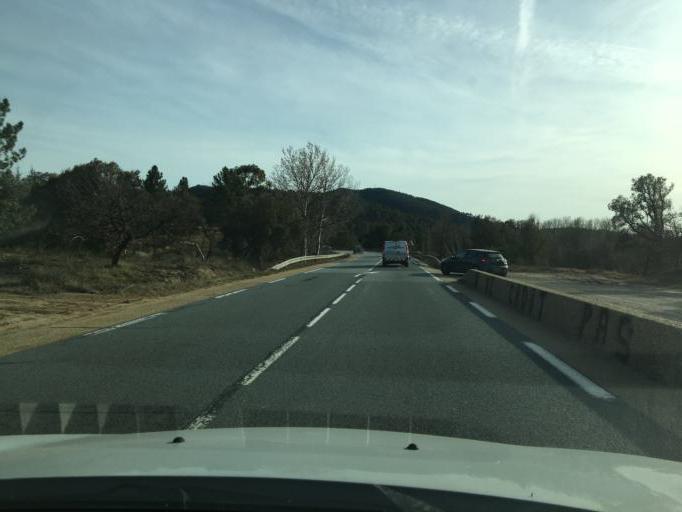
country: FR
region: Provence-Alpes-Cote d'Azur
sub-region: Departement du Var
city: Montauroux
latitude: 43.5550
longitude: 6.7961
